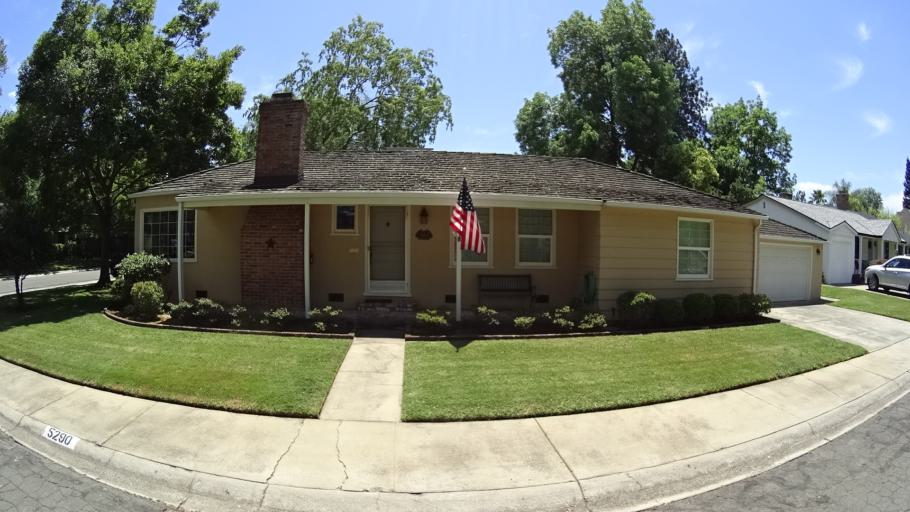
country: US
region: California
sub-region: Sacramento County
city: Sacramento
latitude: 38.5674
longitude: -121.4381
